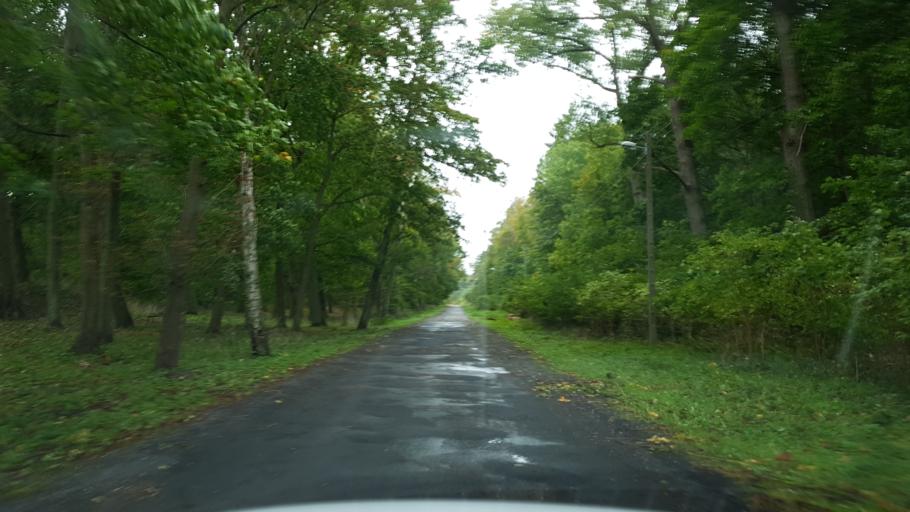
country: PL
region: West Pomeranian Voivodeship
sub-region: Powiat kamienski
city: Wolin
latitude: 53.8345
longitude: 14.6074
